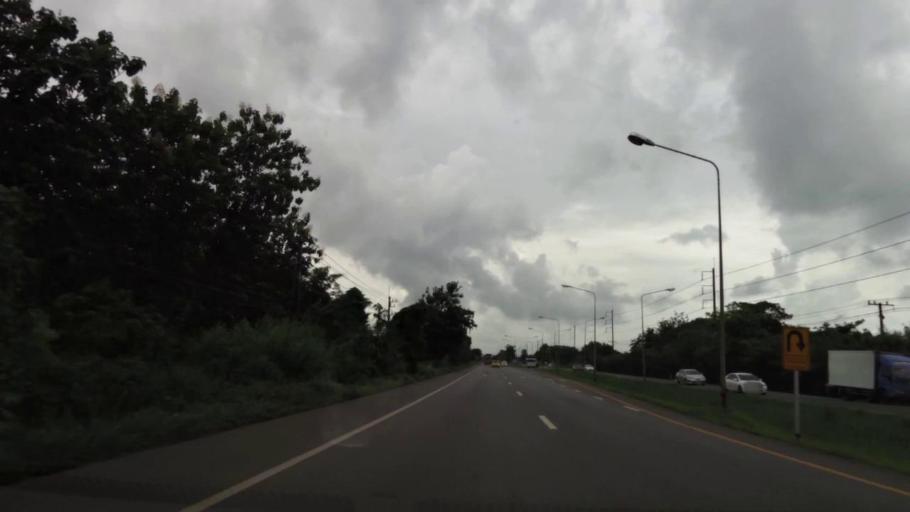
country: TH
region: Chanthaburi
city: Tha Mai
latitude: 12.6909
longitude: 101.9958
